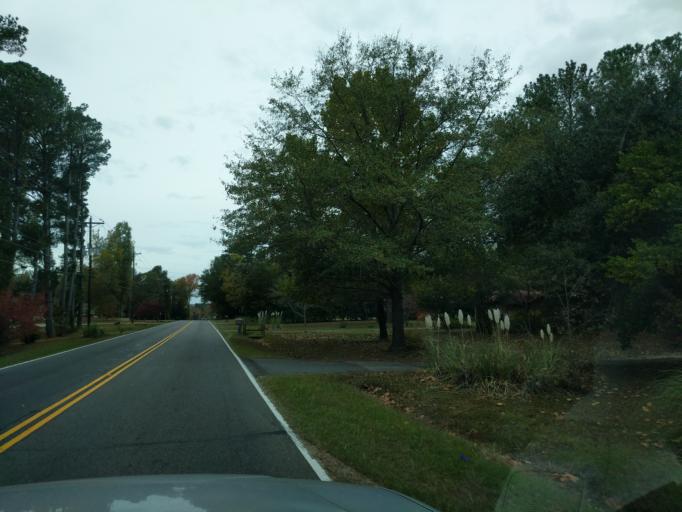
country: US
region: South Carolina
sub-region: Lexington County
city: Batesburg
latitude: 33.9121
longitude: -81.5602
